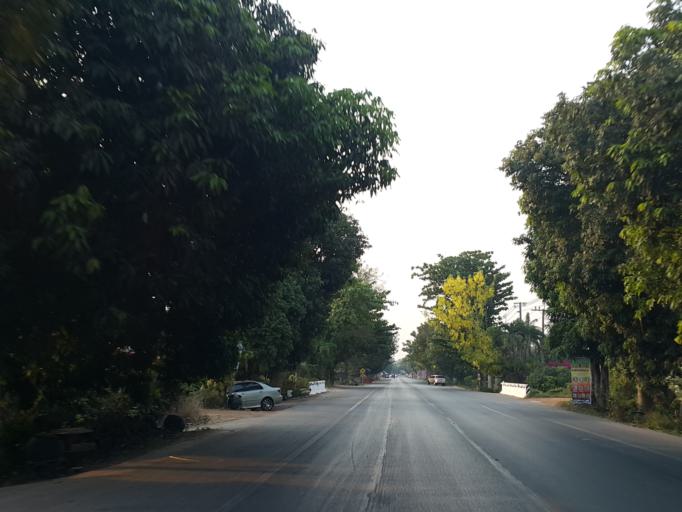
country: TH
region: Sukhothai
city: Si Samrong
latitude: 17.2211
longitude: 99.8619
